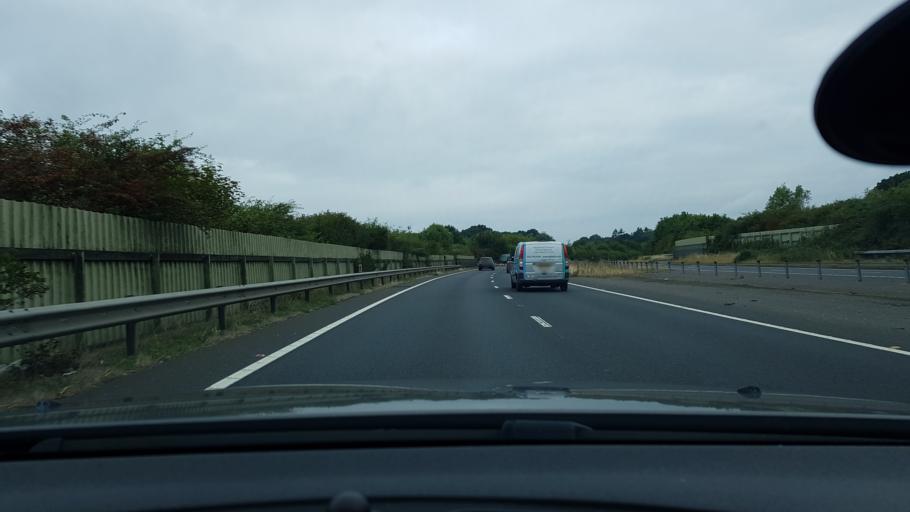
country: GB
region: England
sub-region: Hampshire
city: Highclere
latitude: 51.3675
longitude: -1.3643
